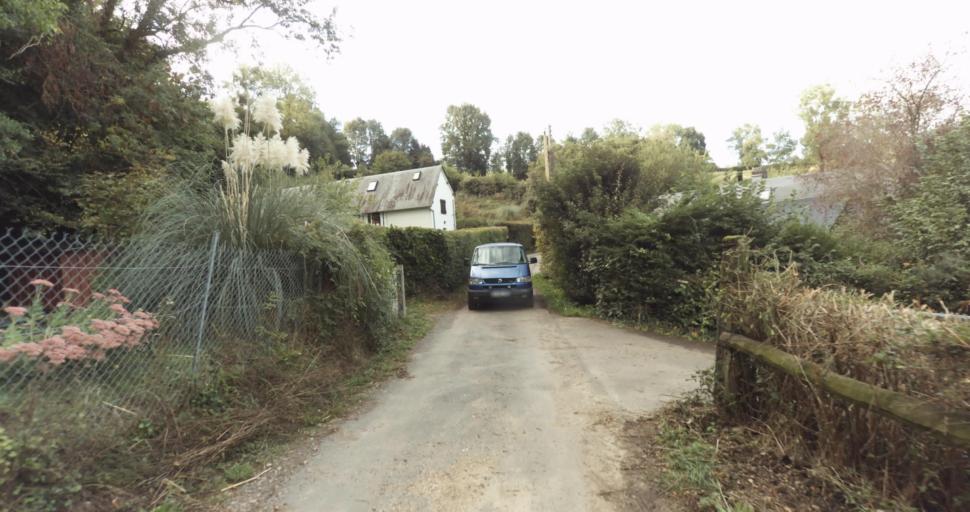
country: FR
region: Lower Normandy
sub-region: Departement de l'Orne
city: Vimoutiers
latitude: 48.8899
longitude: 0.2330
